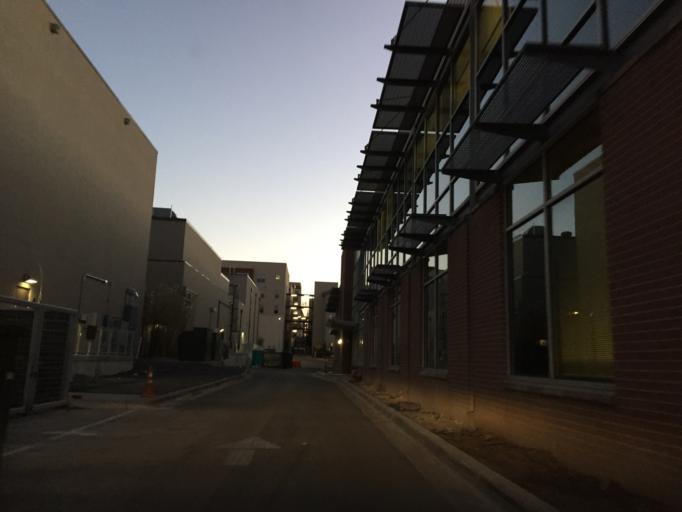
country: US
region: Texas
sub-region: Travis County
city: Wells Branch
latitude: 30.4015
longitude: -97.7231
